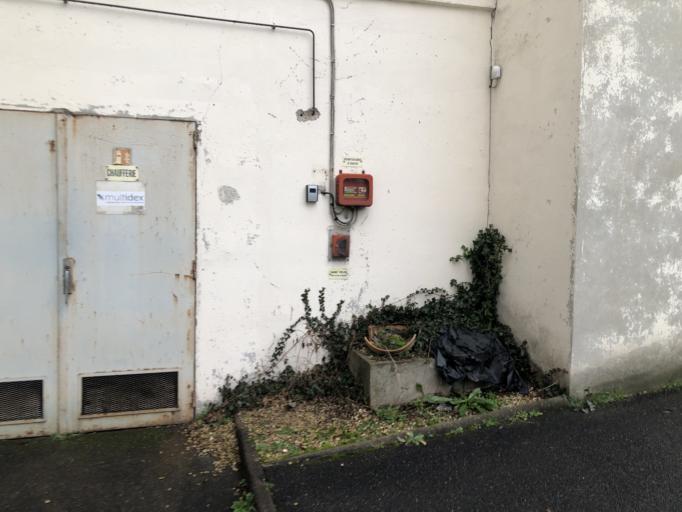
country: FR
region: Ile-de-France
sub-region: Departement de l'Essonne
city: Bures-sur-Yvette
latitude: 48.6973
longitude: 2.1709
